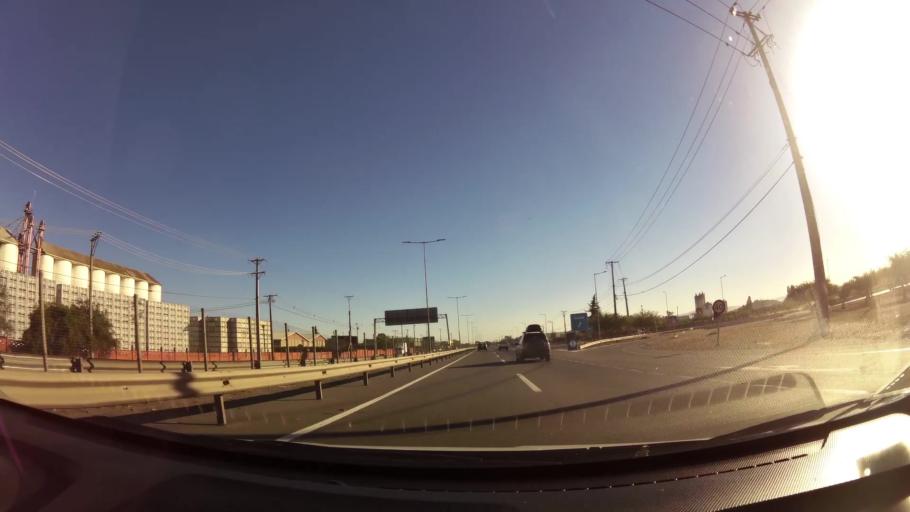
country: CL
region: Maule
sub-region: Provincia de Curico
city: Curico
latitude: -34.9649
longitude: -71.1944
